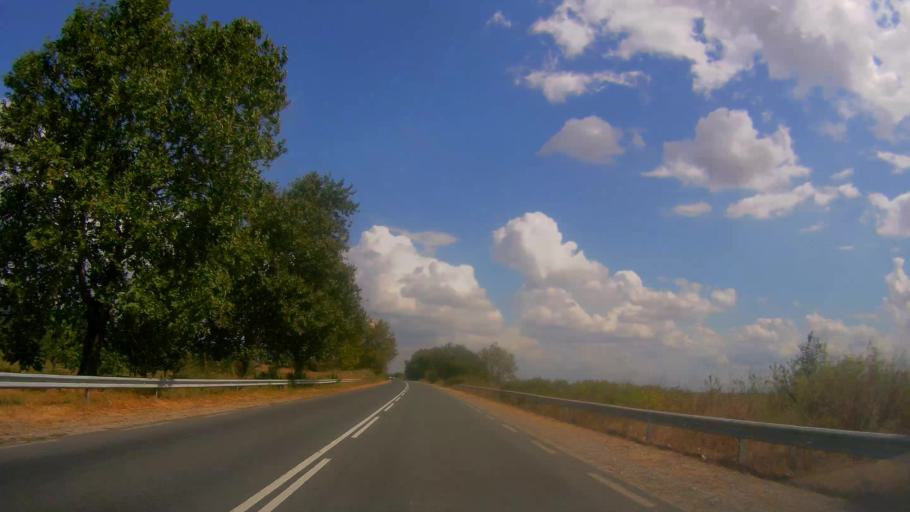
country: BG
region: Sliven
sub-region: Obshtina Sliven
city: Kermen
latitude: 42.6309
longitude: 26.1845
